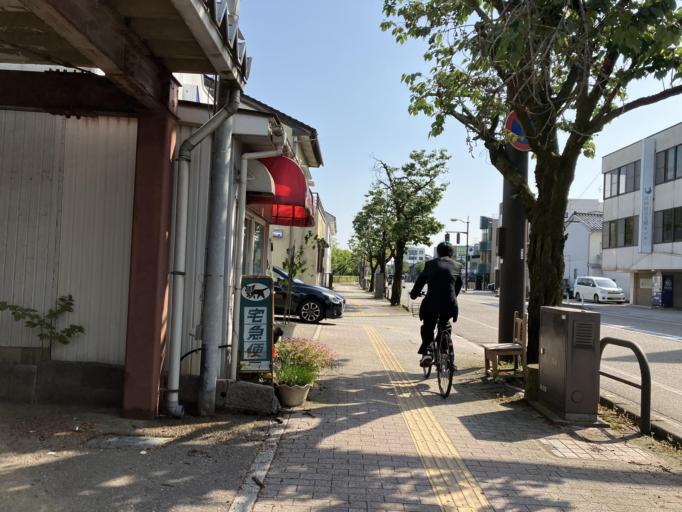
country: JP
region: Toyama
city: Takaoka
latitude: 36.7452
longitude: 137.0205
